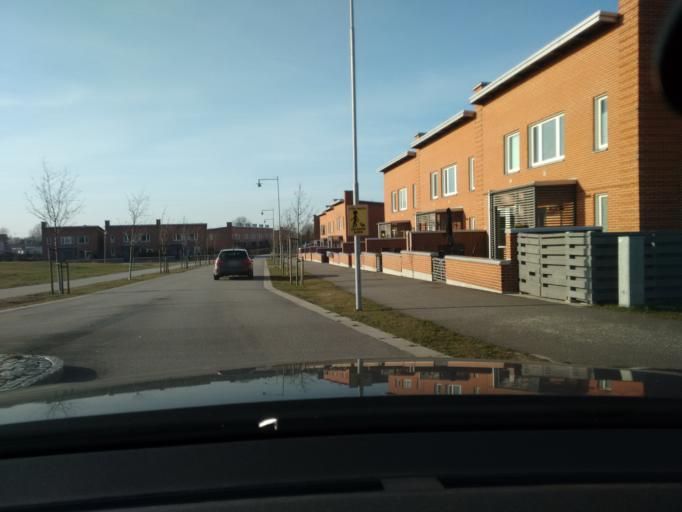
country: SE
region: Skane
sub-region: Lunds Kommun
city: Lund
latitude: 55.7499
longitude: 13.2048
